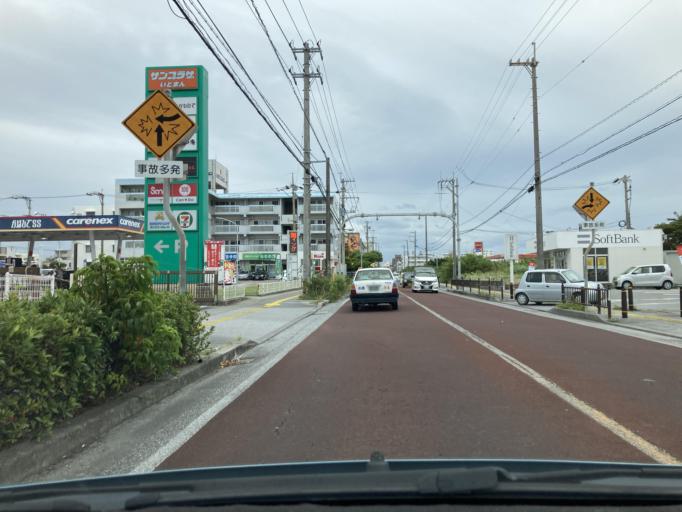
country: JP
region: Okinawa
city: Itoman
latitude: 26.1399
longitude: 127.6714
